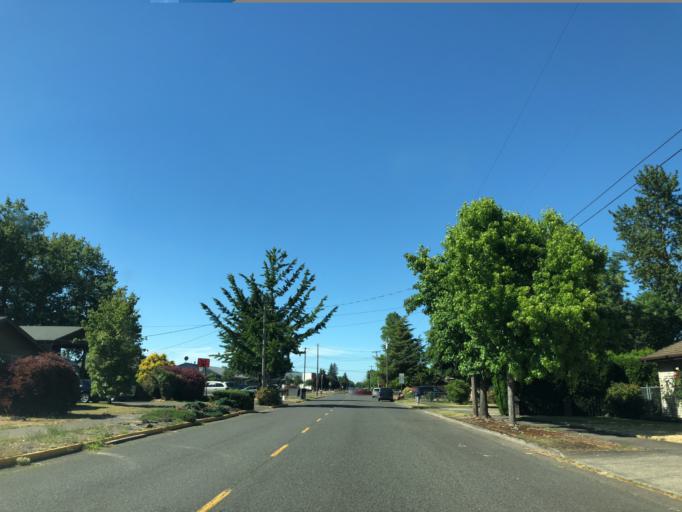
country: US
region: Oregon
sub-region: Linn County
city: Lebanon
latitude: 44.5255
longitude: -122.9127
